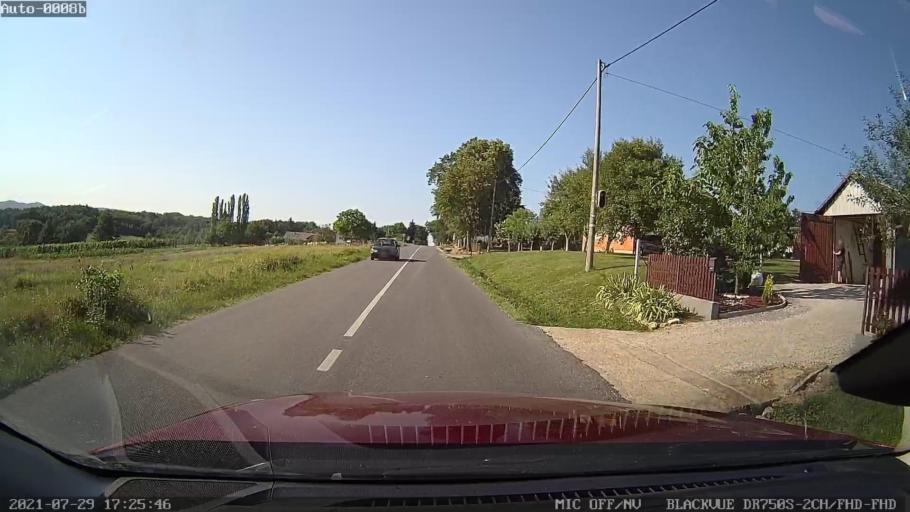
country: HR
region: Varazdinska
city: Ivanec
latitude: 46.2492
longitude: 16.1183
